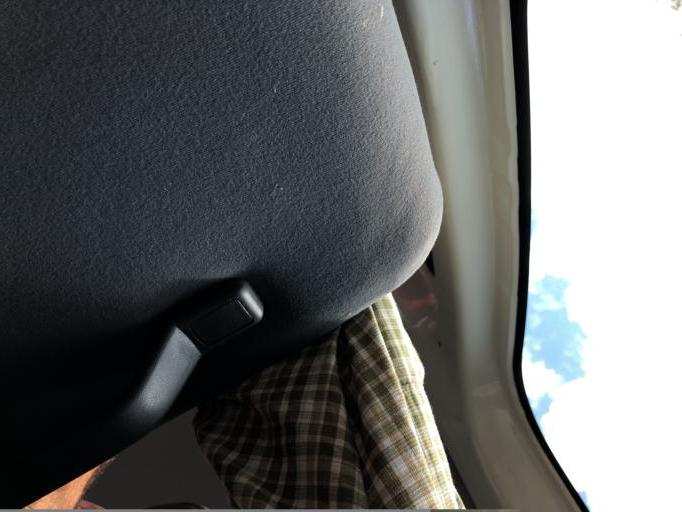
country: ET
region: Adis Abeba
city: Addis Ababa
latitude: 9.0076
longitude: 38.7811
